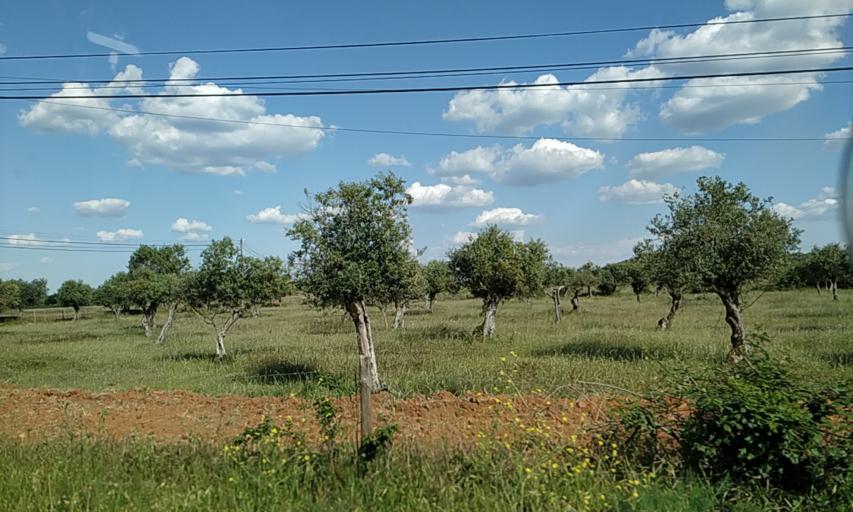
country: PT
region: Evora
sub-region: Estremoz
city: Estremoz
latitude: 38.8583
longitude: -7.5773
